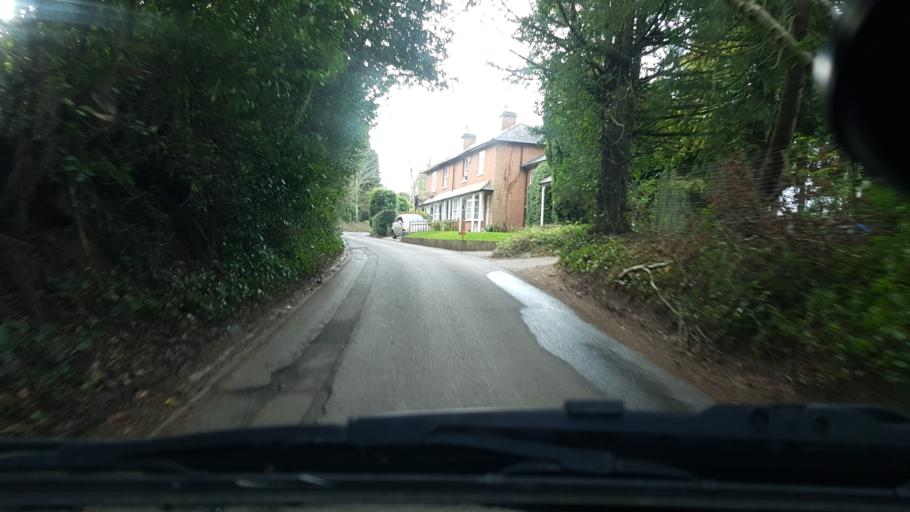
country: GB
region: England
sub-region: Surrey
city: Cobham
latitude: 51.3087
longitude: -0.4332
